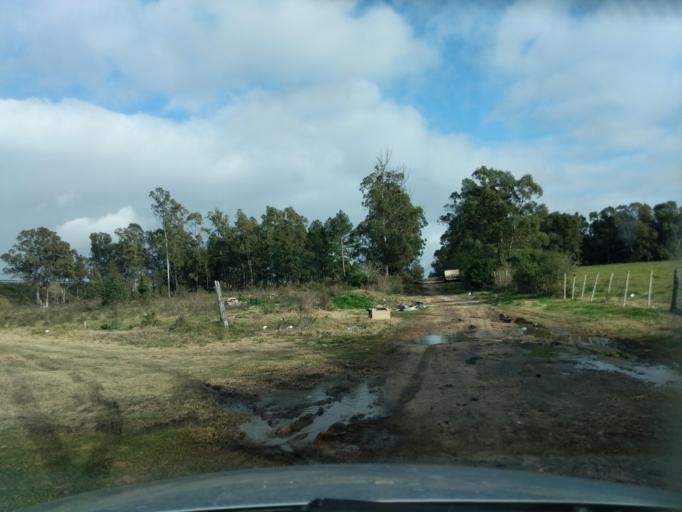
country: UY
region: Florida
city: Florida
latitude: -34.0763
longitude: -56.2280
